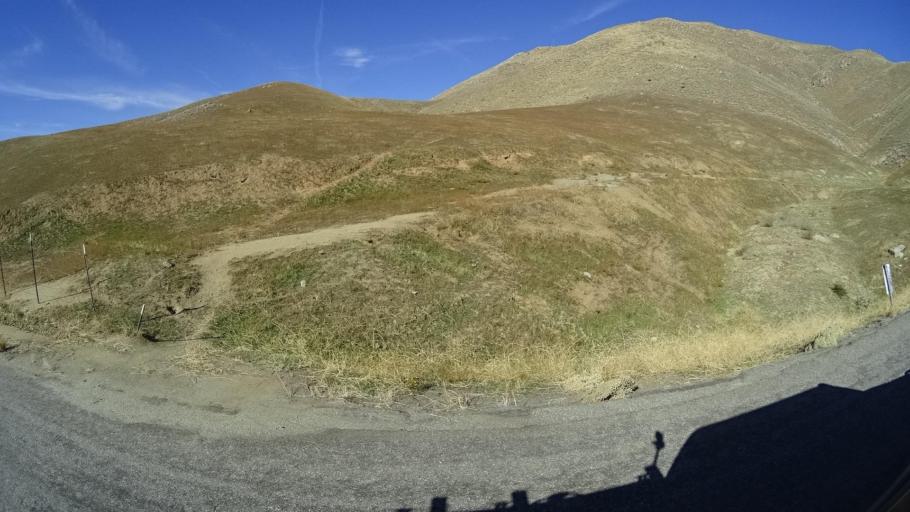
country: US
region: California
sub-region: Kern County
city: Arvin
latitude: 35.4215
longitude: -118.7425
